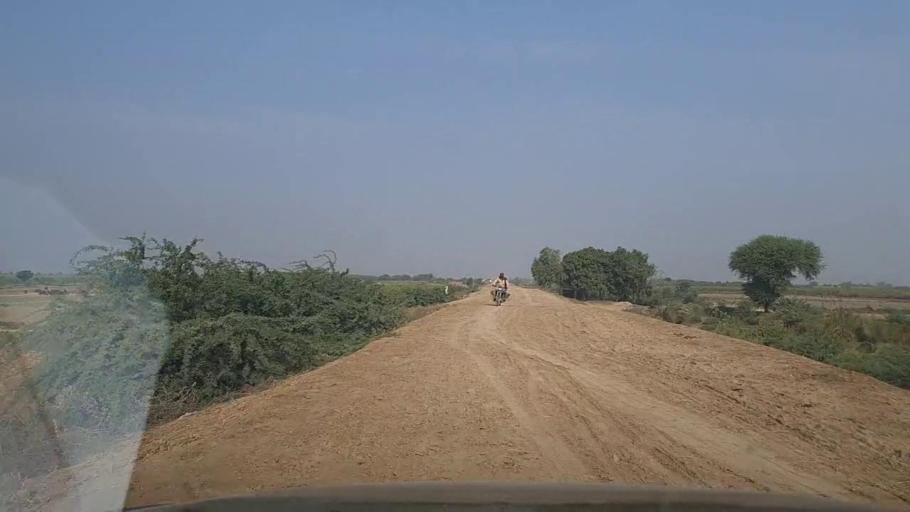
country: PK
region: Sindh
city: Bulri
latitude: 24.9965
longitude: 68.2905
